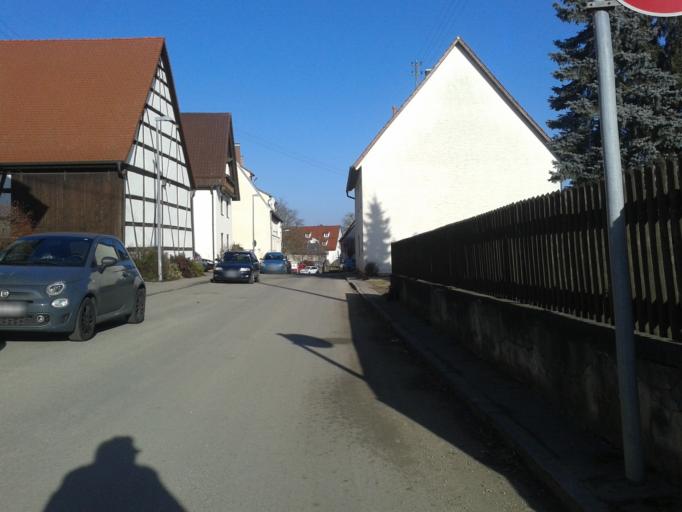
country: DE
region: Baden-Wuerttemberg
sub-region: Tuebingen Region
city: Ulm
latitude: 48.3711
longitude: 9.9347
